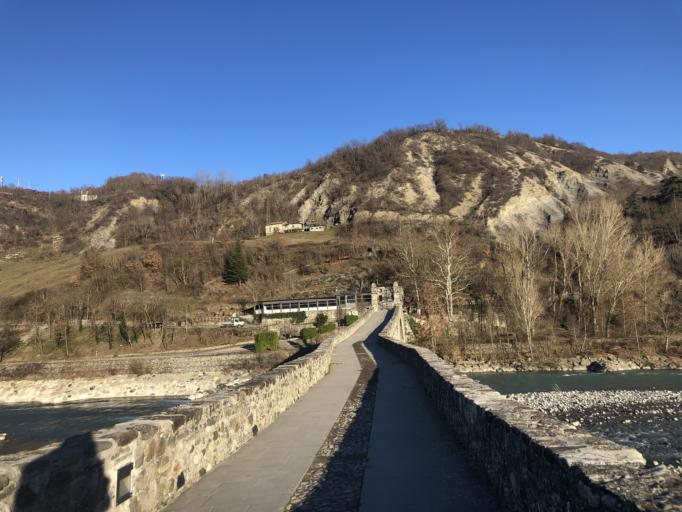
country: IT
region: Emilia-Romagna
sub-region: Provincia di Piacenza
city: Bobbio
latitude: 44.7672
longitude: 9.3910
